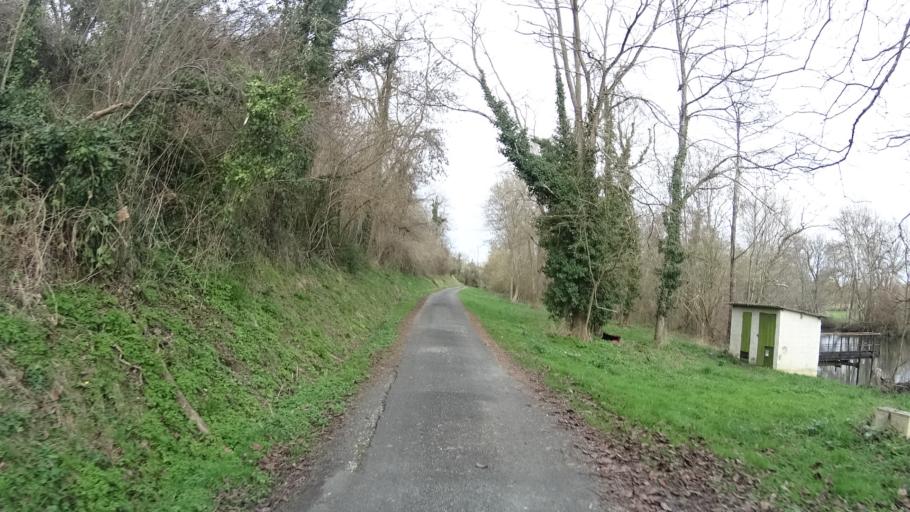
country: FR
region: Aquitaine
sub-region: Departement de la Dordogne
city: Saint-Aulaye
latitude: 45.2453
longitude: 0.1504
